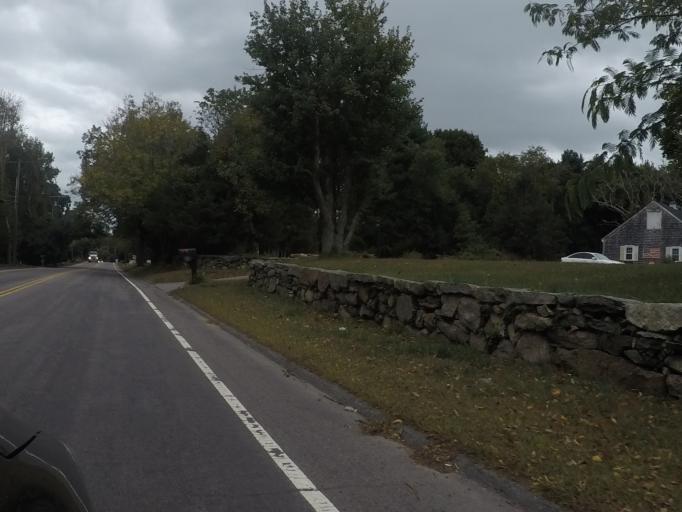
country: US
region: Massachusetts
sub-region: Bristol County
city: Smith Mills
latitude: 41.6256
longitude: -70.9964
